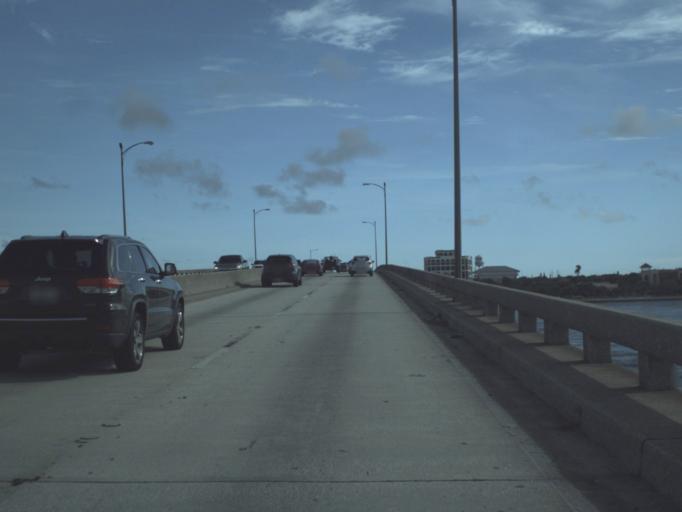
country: US
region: Florida
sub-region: Manatee County
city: Bradenton
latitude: 27.5056
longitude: -82.5631
